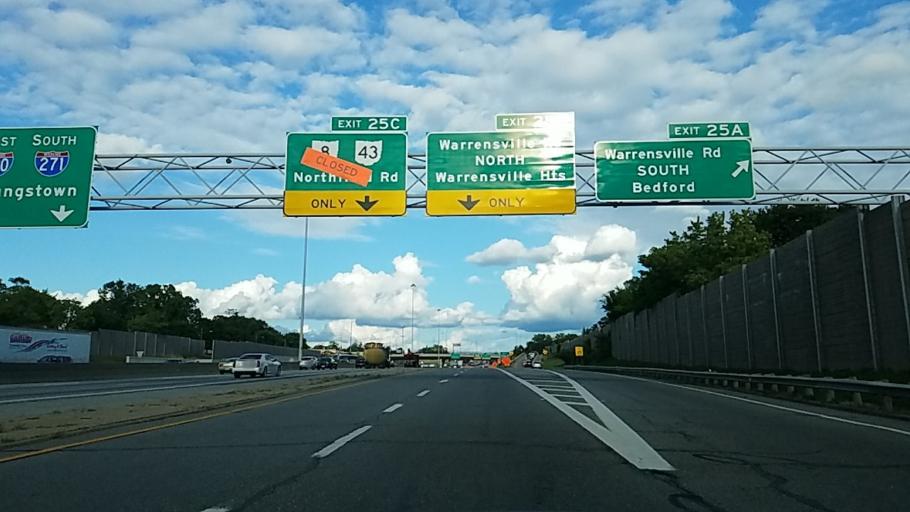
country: US
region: Ohio
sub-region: Cuyahoga County
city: Warrensville Heights
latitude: 41.4246
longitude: -81.5428
